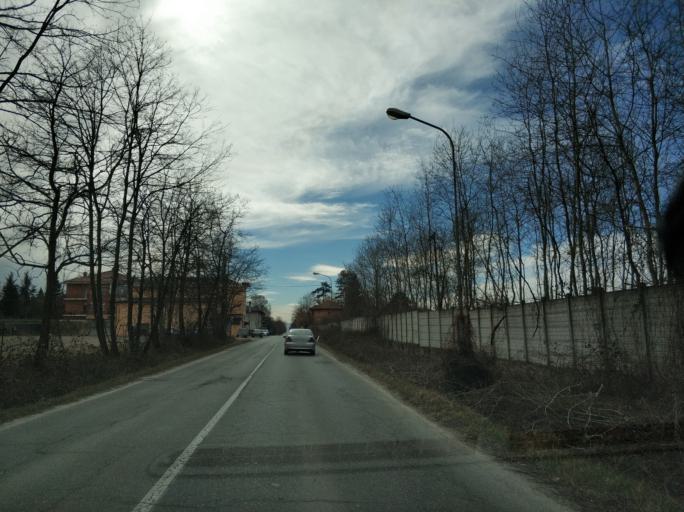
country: IT
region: Piedmont
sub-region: Provincia di Torino
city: Lombardore
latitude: 45.2248
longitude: 7.7314
